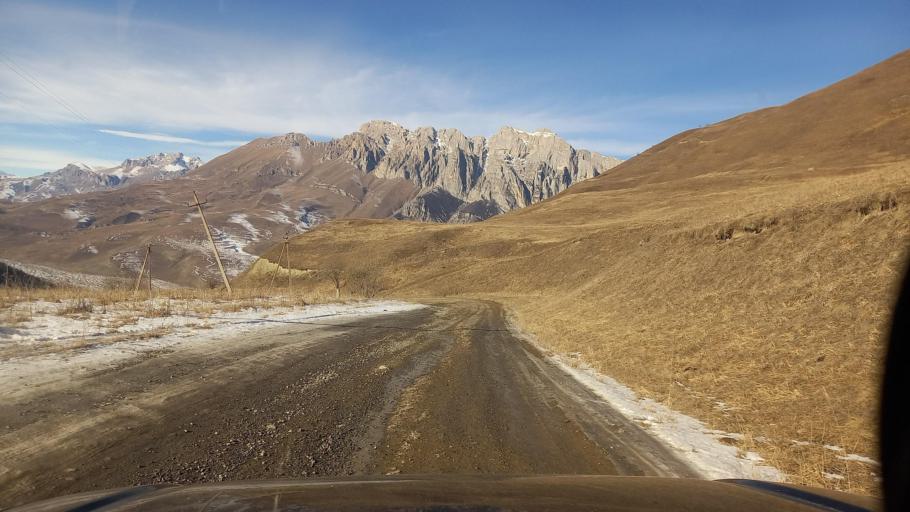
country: RU
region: North Ossetia
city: Verkhniy Fiagdon
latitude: 42.8349
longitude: 44.4777
